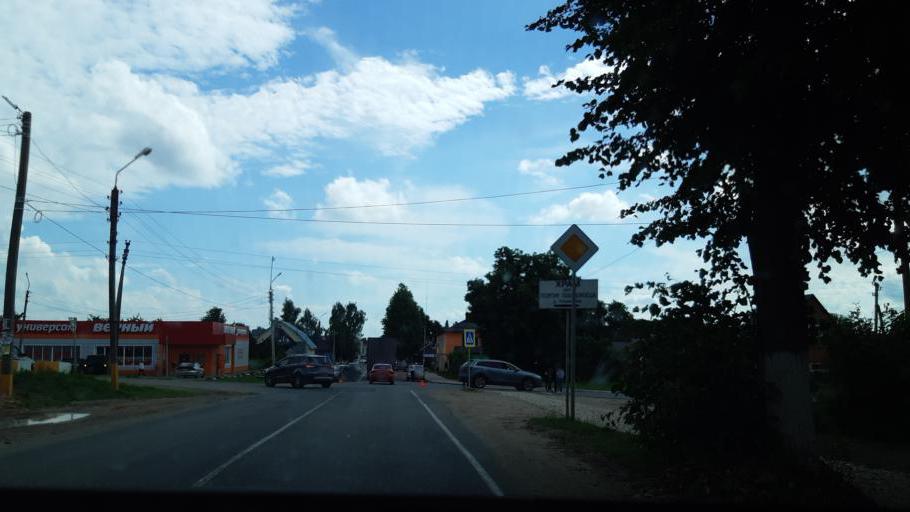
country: RU
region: Kaluga
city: Medyn'
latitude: 54.9717
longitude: 35.8588
